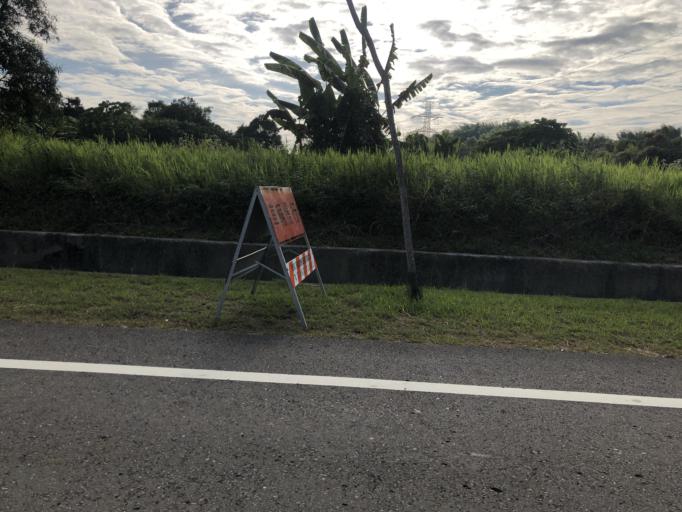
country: TW
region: Taiwan
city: Yujing
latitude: 23.0482
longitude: 120.4230
